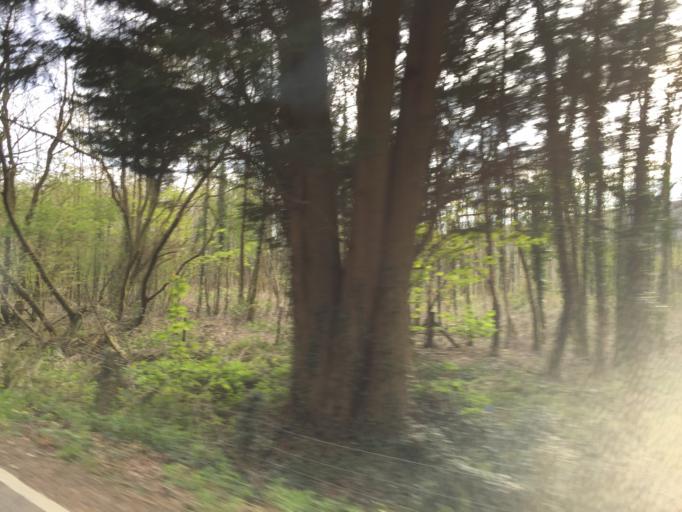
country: GB
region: Wales
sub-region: Caerphilly County Borough
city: Llanbradach
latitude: 51.5999
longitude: -3.2256
